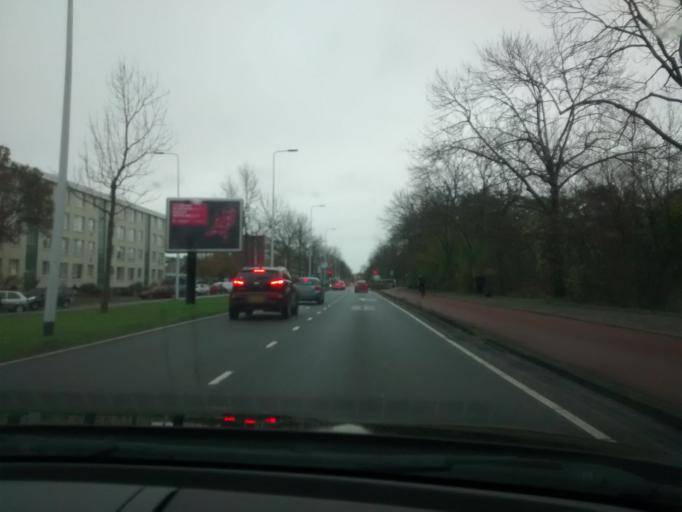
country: NL
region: South Holland
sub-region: Gemeente Leiden
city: Leiden
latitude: 52.1484
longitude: 4.4749
